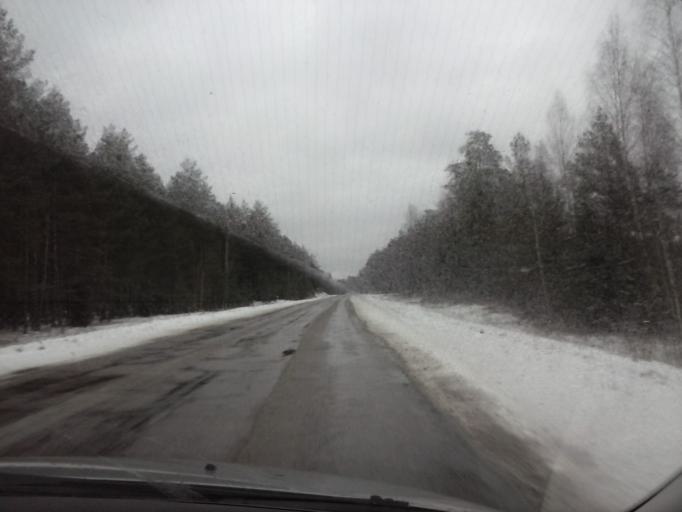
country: LV
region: Strenci
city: Seda
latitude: 57.6710
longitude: 25.8797
